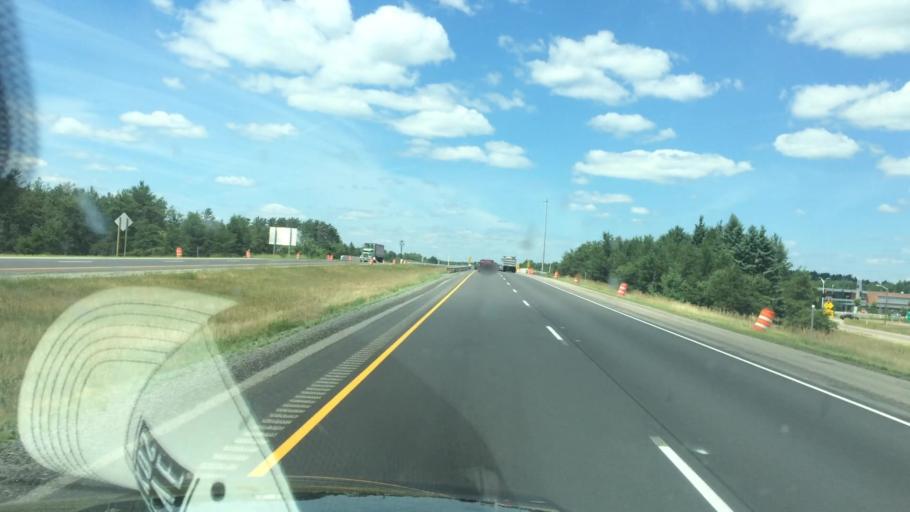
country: US
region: Wisconsin
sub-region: Portage County
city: Stevens Point
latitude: 44.5392
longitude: -89.5428
